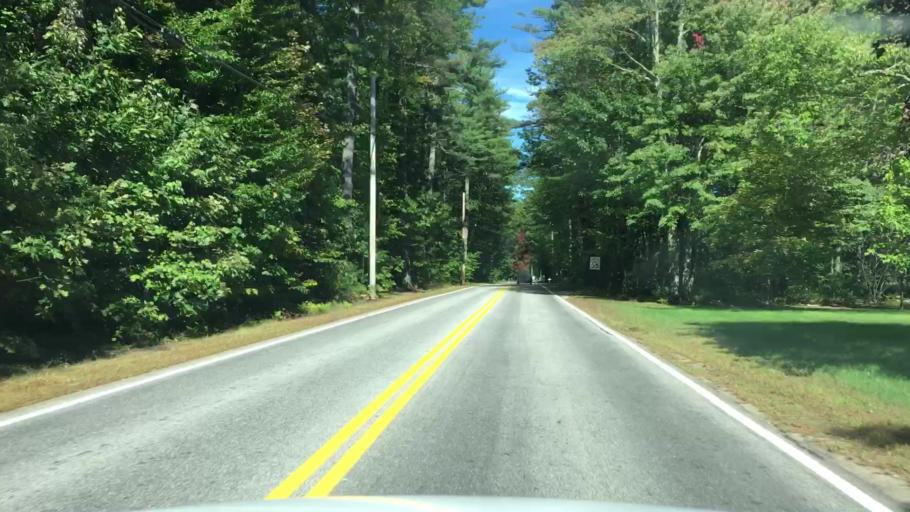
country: US
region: Maine
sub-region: Cumberland County
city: West Scarborough
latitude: 43.5944
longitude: -70.4308
